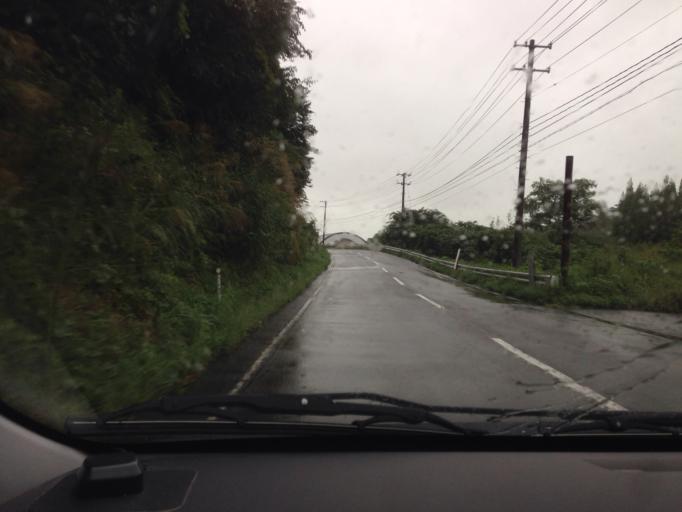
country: JP
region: Fukushima
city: Koriyama
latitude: 37.4435
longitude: 140.2653
